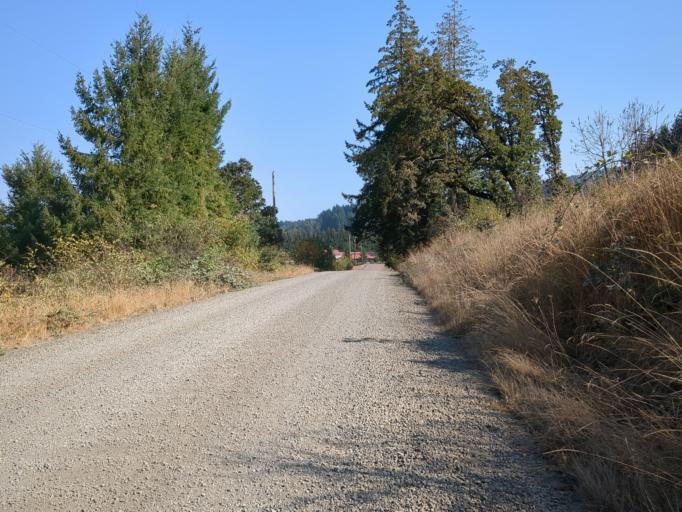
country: US
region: Oregon
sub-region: Lane County
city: Junction City
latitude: 44.2952
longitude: -123.3619
